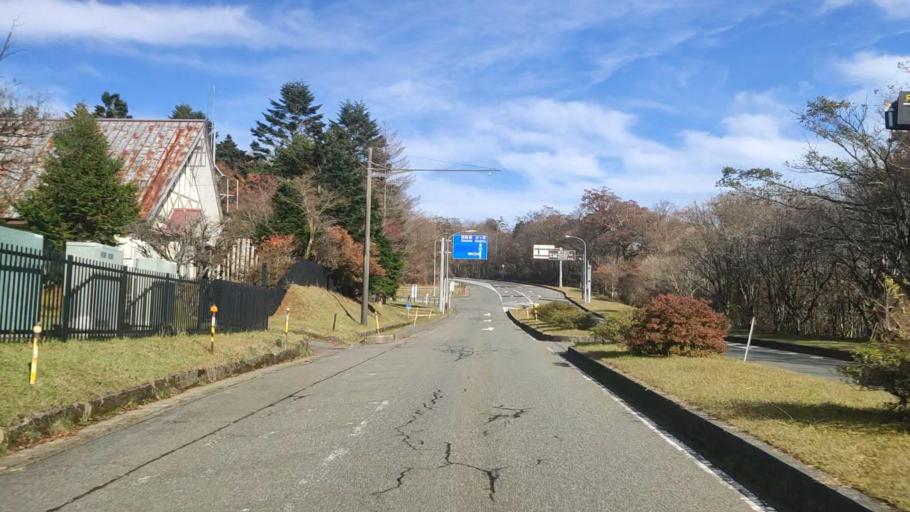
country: JP
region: Shizuoka
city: Fuji
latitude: 35.3025
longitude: 138.7490
